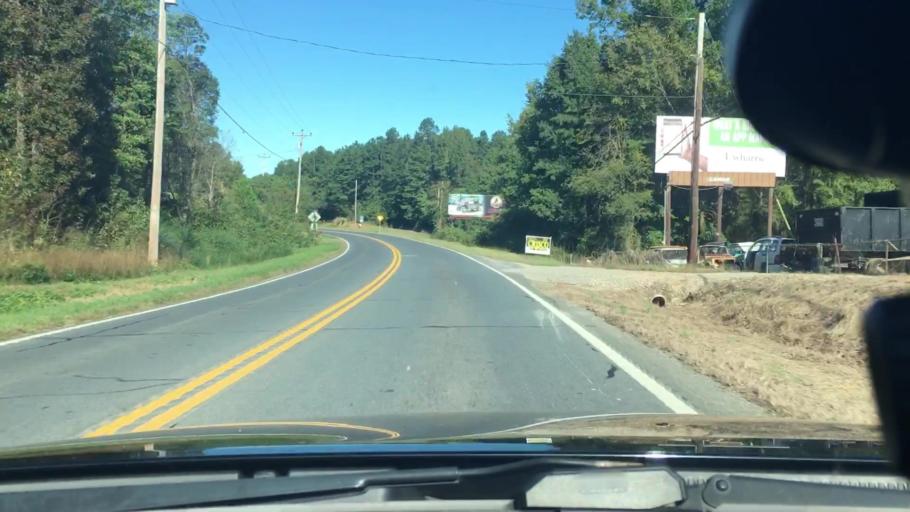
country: US
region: North Carolina
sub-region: Stanly County
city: Albemarle
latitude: 35.3422
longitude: -80.1406
